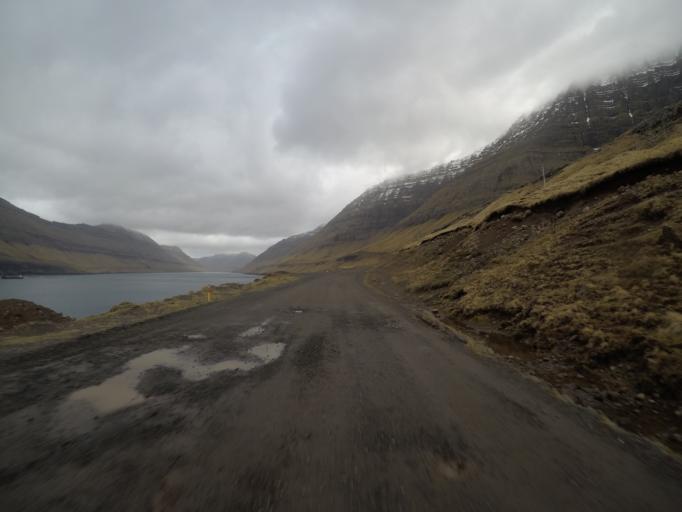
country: FO
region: Nordoyar
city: Klaksvik
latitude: 62.3457
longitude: -6.5798
